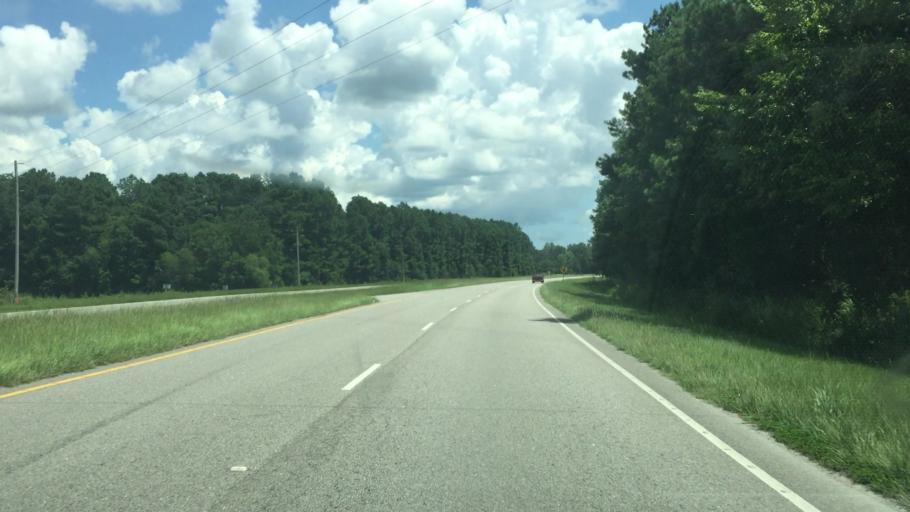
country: US
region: South Carolina
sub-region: Horry County
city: Loris
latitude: 34.0077
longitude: -78.7651
